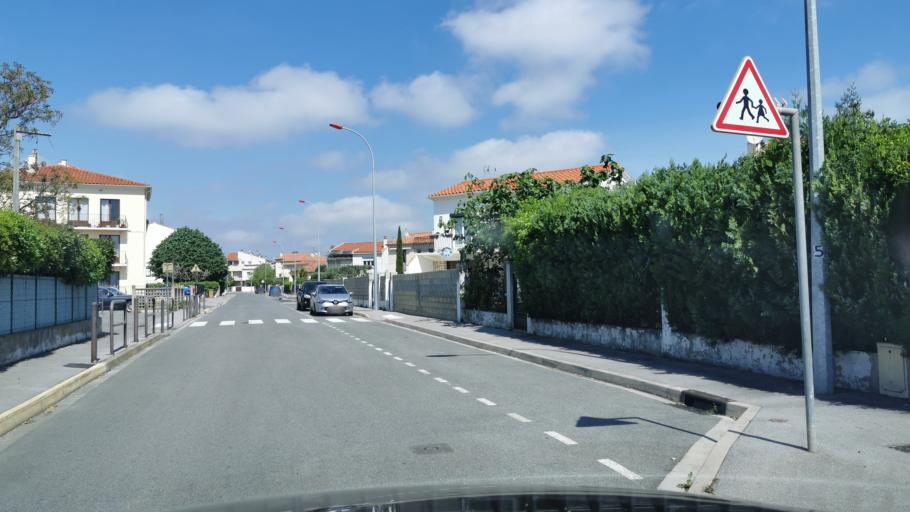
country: FR
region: Languedoc-Roussillon
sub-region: Departement de l'Aude
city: Narbonne
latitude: 43.1838
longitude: 3.0173
